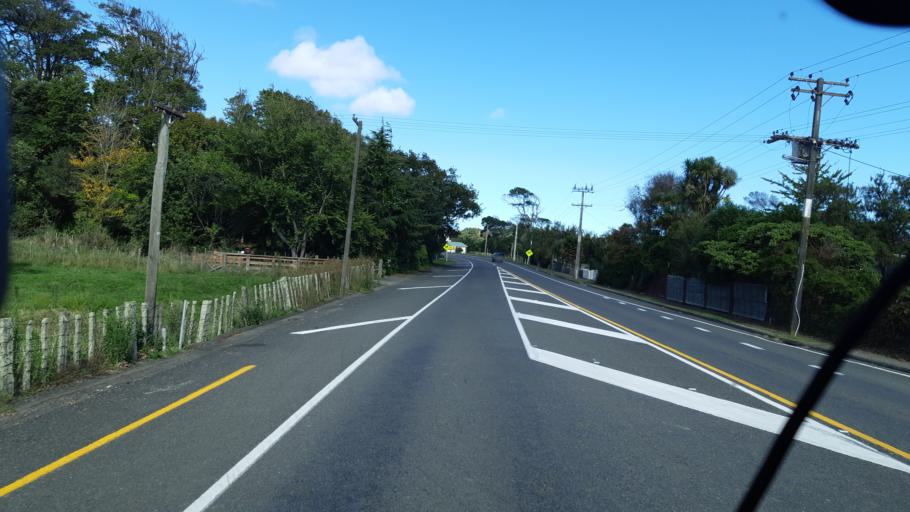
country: NZ
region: Manawatu-Wanganui
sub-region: Wanganui District
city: Wanganui
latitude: -40.0411
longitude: 175.2120
